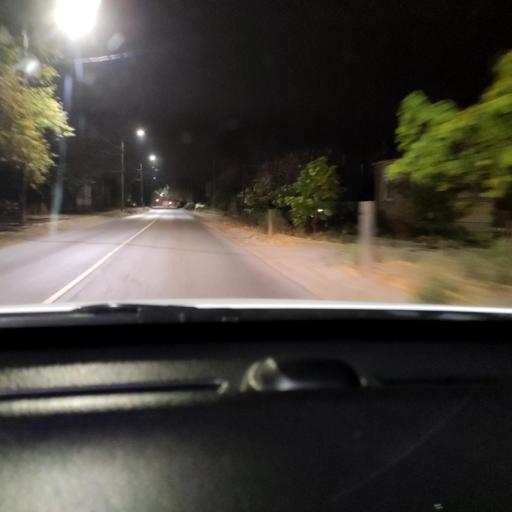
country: RU
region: Voronezj
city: Somovo
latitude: 51.7384
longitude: 39.2671
